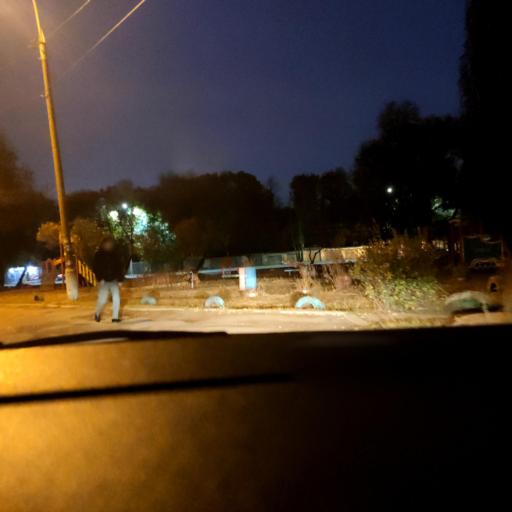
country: RU
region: Voronezj
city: Voronezh
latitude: 51.7029
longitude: 39.1718
